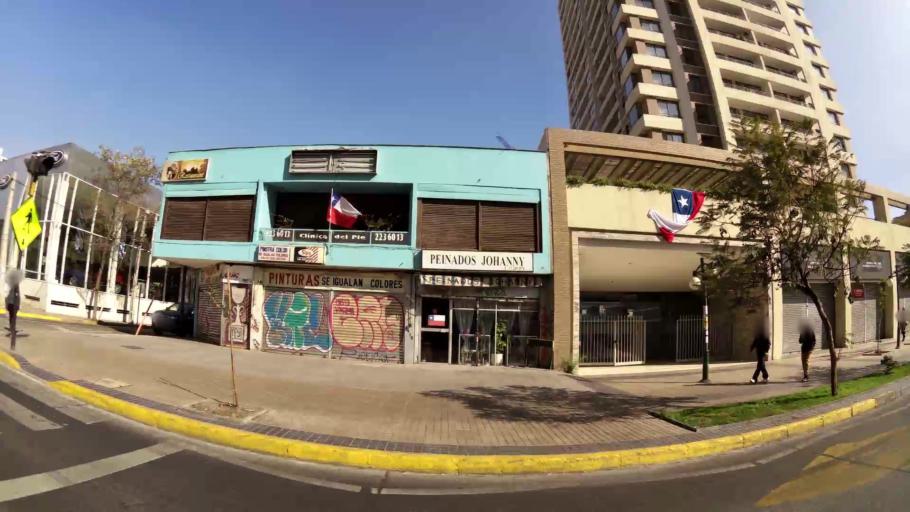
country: CL
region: Santiago Metropolitan
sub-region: Provincia de Santiago
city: Santiago
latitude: -33.4532
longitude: -70.6161
